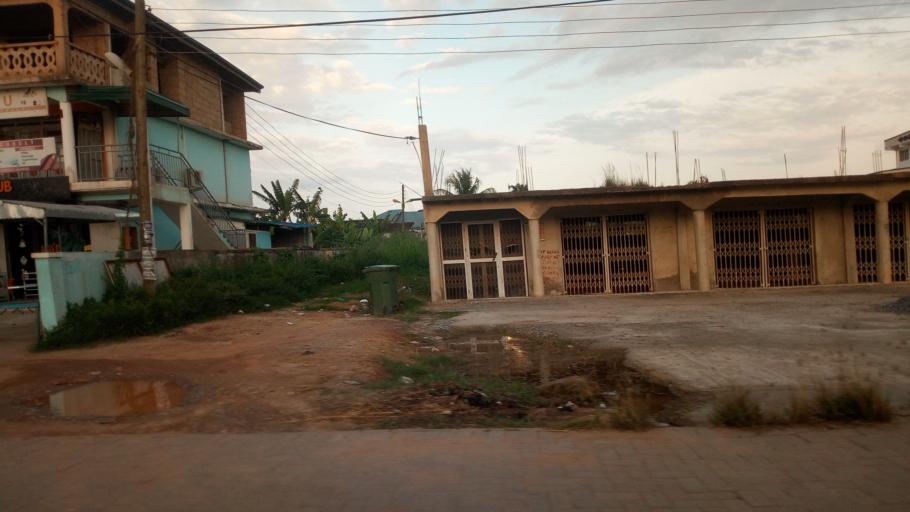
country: GH
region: Western
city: Takoradi
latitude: 4.9308
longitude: -1.7802
